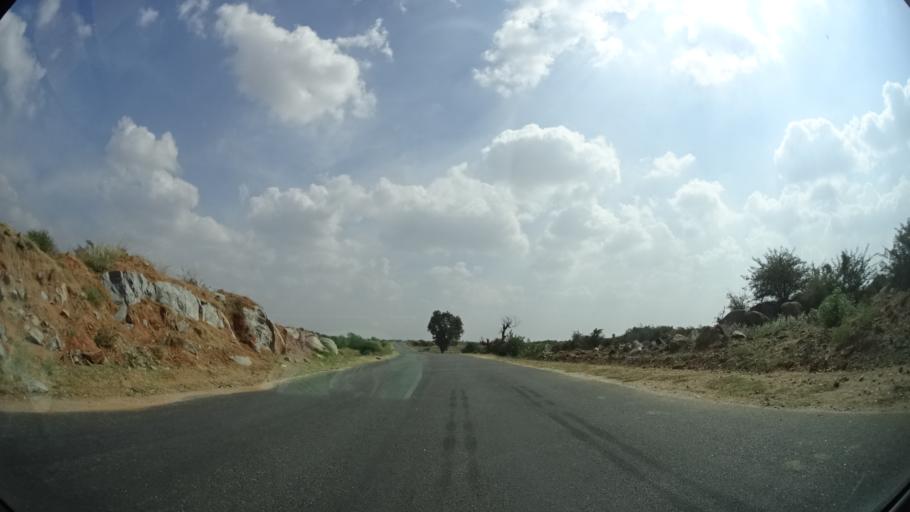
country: IN
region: Andhra Pradesh
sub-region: Anantapur
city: Uravakonda
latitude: 14.8198
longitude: 77.3426
